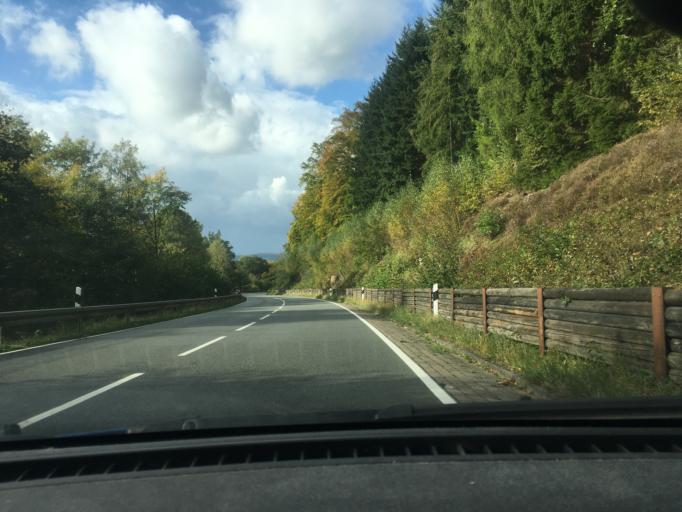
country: DE
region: Lower Saxony
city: Bevern
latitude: 51.8136
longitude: 9.4929
